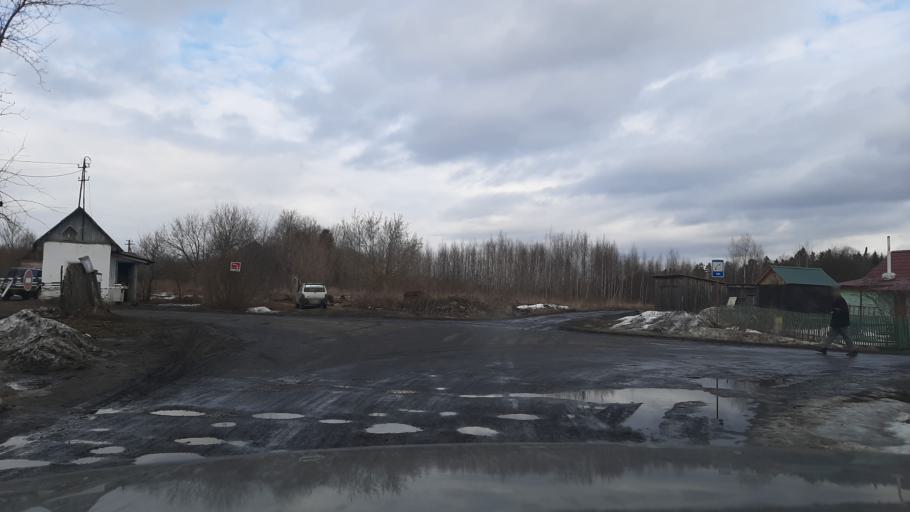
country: RU
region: Ivanovo
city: Teykovo
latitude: 56.8980
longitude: 40.6642
